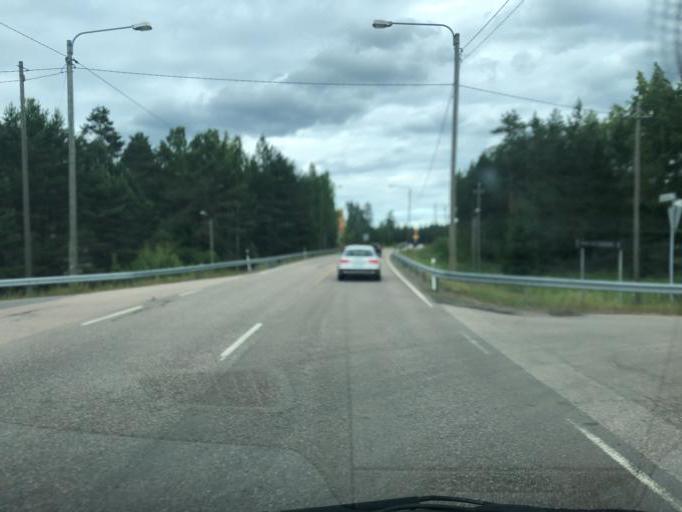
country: FI
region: Southern Savonia
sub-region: Mikkeli
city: Maentyharju
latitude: 61.0890
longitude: 27.0667
